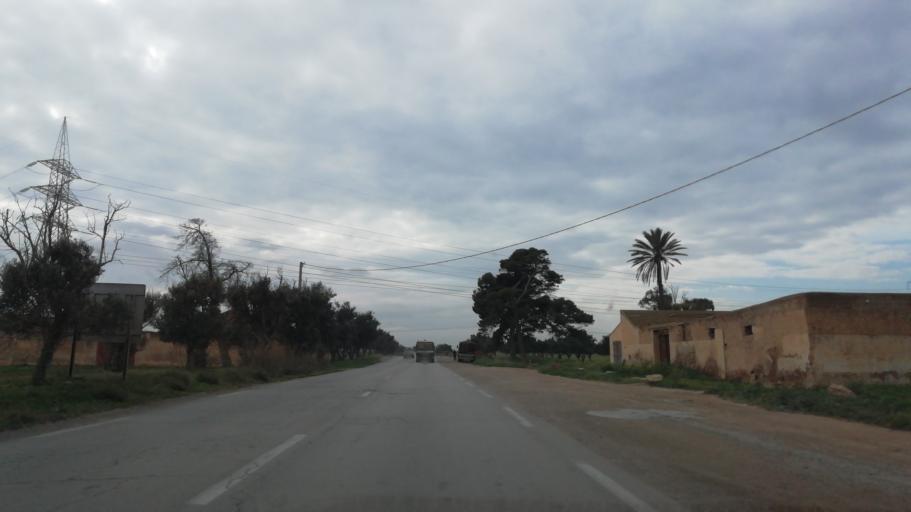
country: DZ
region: Oran
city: Ain el Bya
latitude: 35.7710
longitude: -0.3472
